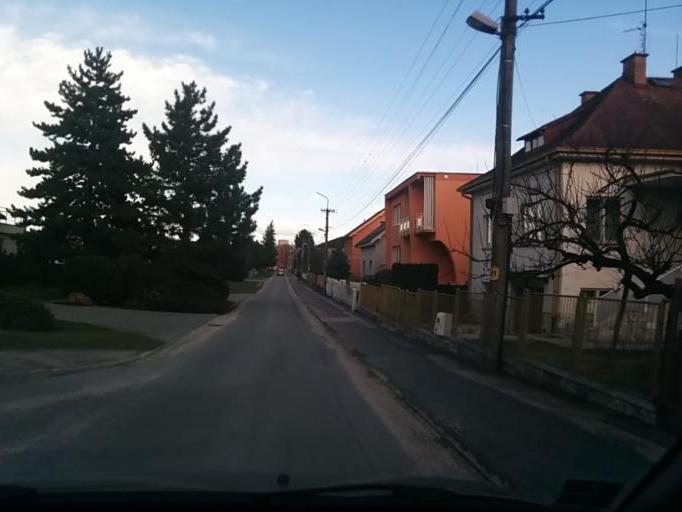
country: SK
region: Trenciansky
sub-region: Okres Nove Mesto nad Vahom
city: Nove Mesto nad Vahom
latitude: 48.7489
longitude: 17.8274
